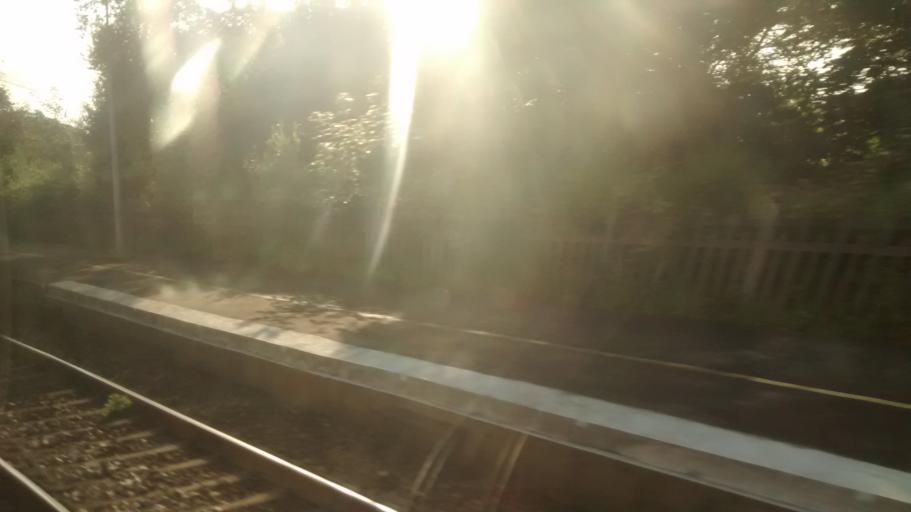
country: FR
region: Brittany
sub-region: Departement d'Ille-et-Vilaine
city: Saint-Didier
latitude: 48.1095
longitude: -1.3208
